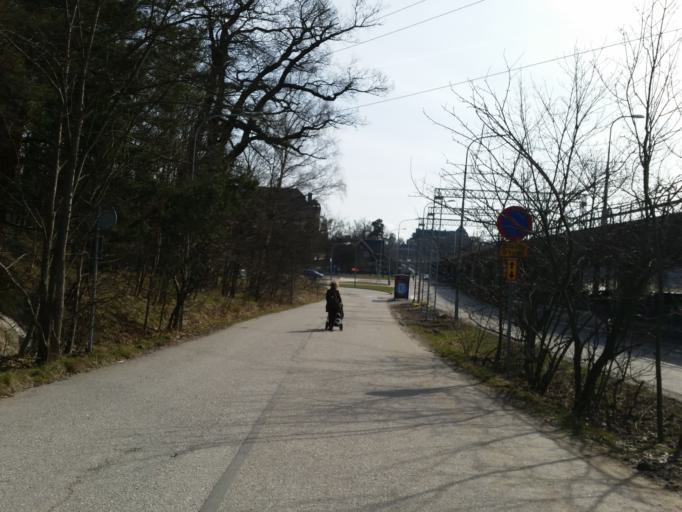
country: SE
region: Stockholm
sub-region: Norrtalje Kommun
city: Bergshamra
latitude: 59.3721
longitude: 18.0508
